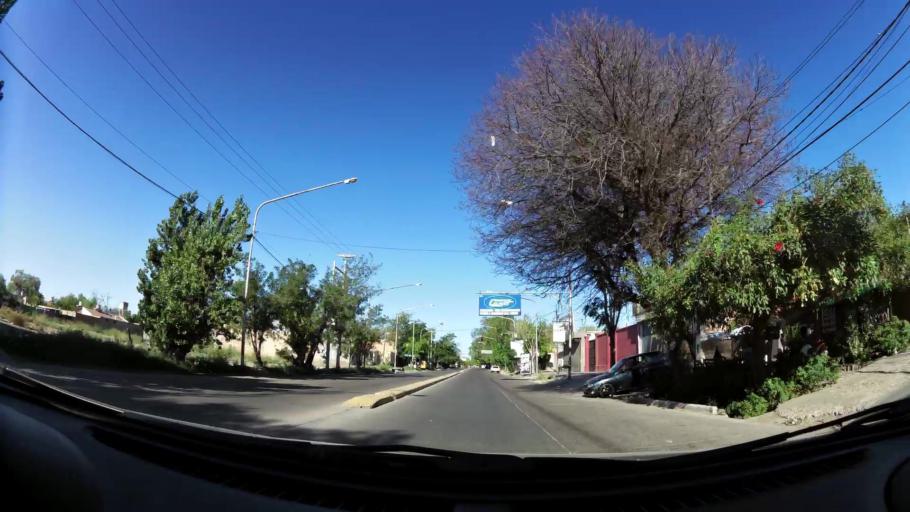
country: AR
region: Mendoza
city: Las Heras
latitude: -32.8422
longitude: -68.8162
